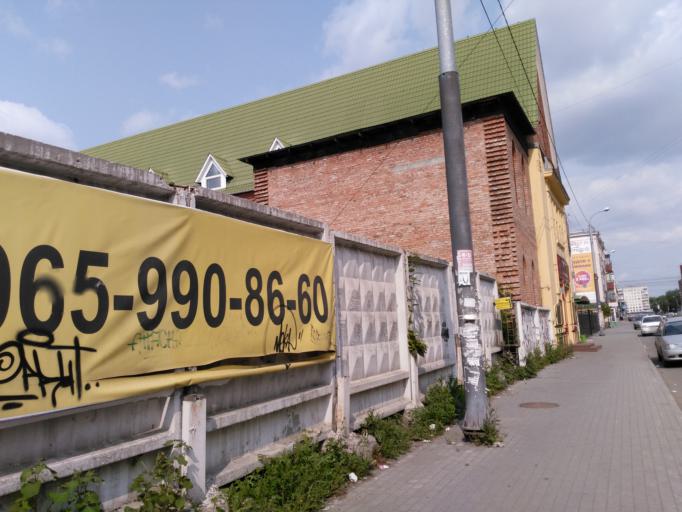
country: RU
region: Chelyabinsk
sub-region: Gorod Chelyabinsk
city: Chelyabinsk
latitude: 55.1656
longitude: 61.4064
